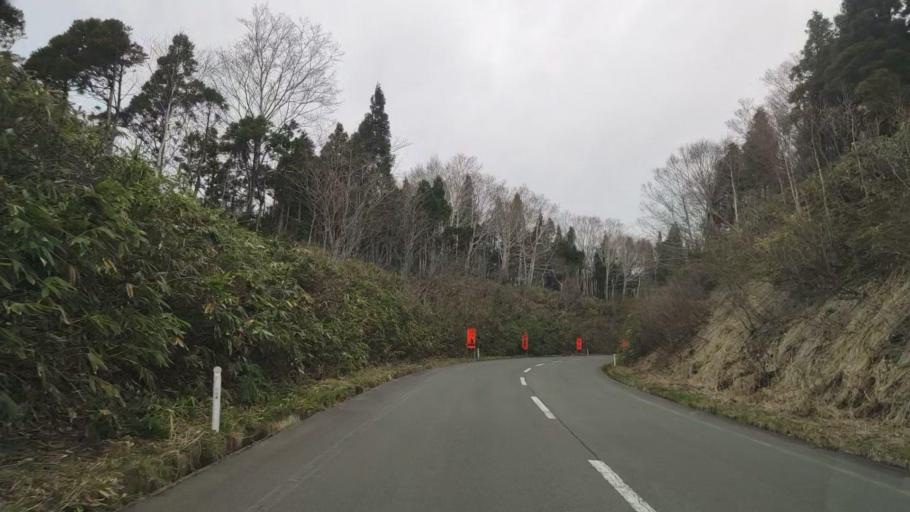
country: JP
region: Akita
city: Hanawa
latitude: 40.4115
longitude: 140.8471
